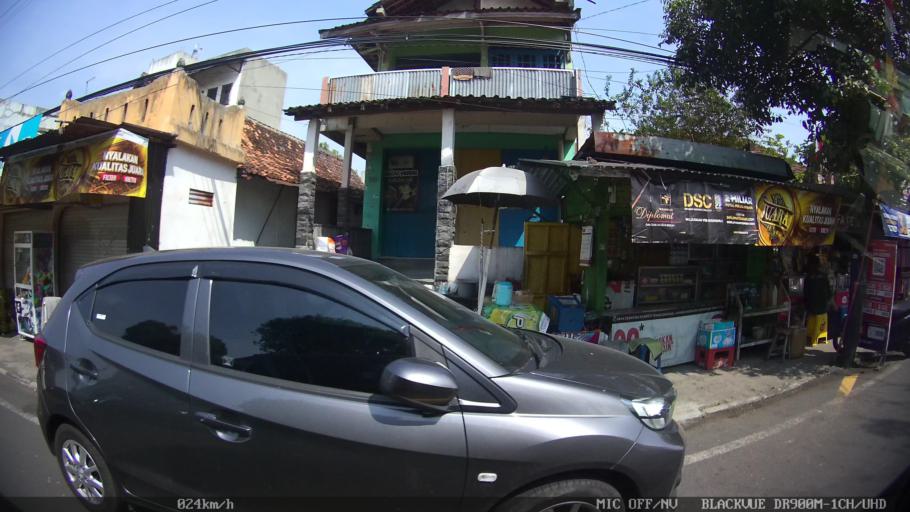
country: ID
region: Daerah Istimewa Yogyakarta
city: Yogyakarta
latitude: -7.7877
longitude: 110.3575
